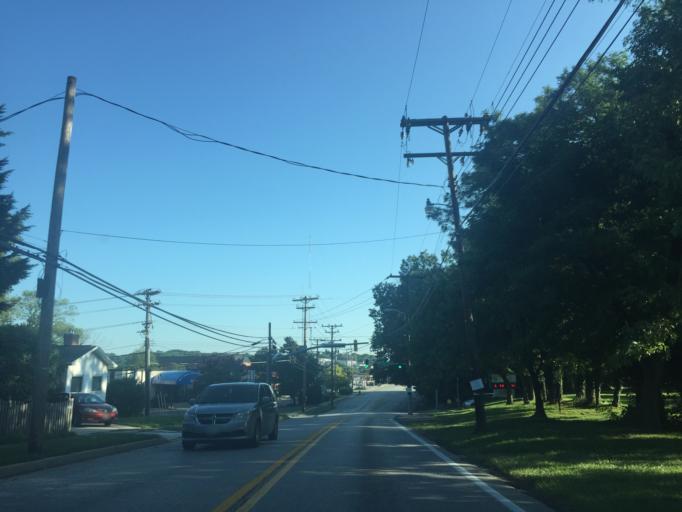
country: US
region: Maryland
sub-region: Baltimore County
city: Catonsville
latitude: 39.2791
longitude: -76.7547
